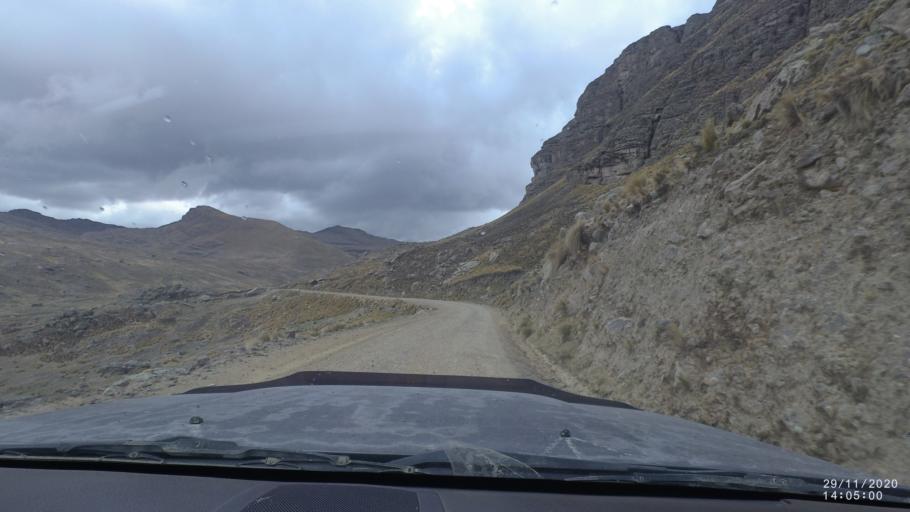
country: BO
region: Cochabamba
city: Sipe Sipe
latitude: -17.2040
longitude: -66.3775
